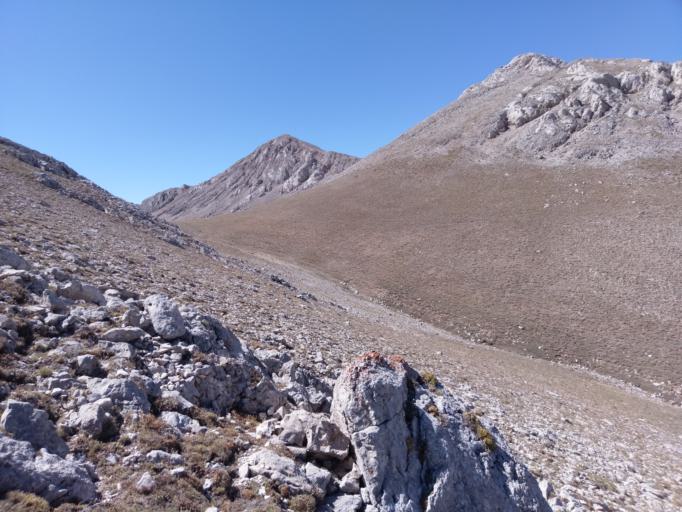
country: TR
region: Adana
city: Tufanbeyli
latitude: 38.3531
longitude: 36.1487
